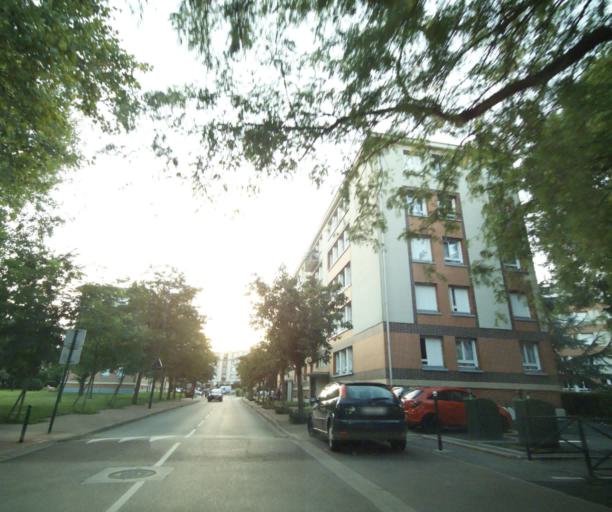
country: FR
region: Ile-de-France
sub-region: Departement des Hauts-de-Seine
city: Le Plessis-Robinson
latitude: 48.7846
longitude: 2.2435
